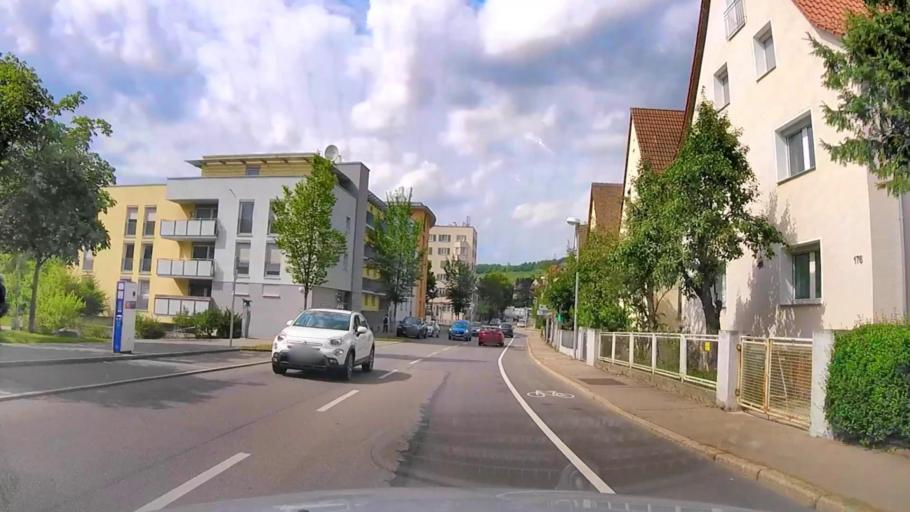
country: DE
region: Baden-Wuerttemberg
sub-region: Regierungsbezirk Stuttgart
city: Stuttgart Feuerbach
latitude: 48.8103
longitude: 9.1506
